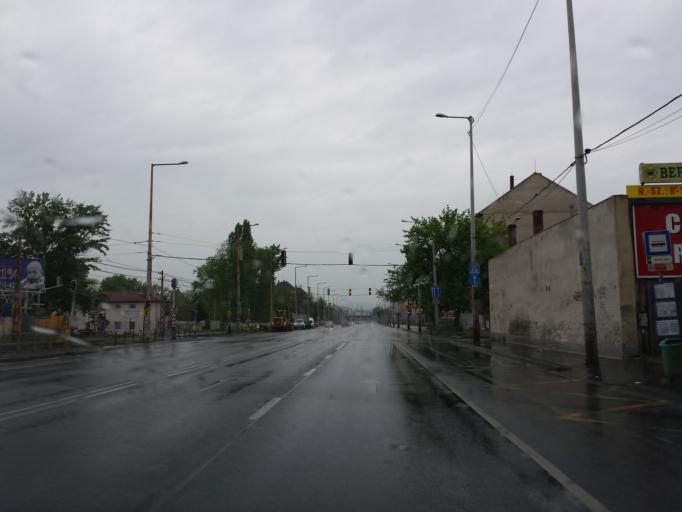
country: HU
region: Budapest
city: Budapest IX. keruelet
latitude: 47.4602
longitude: 19.0825
